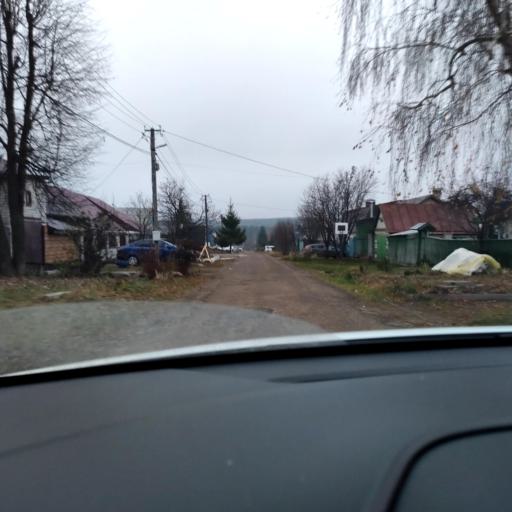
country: RU
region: Tatarstan
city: Staroye Arakchino
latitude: 55.8811
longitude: 49.0494
